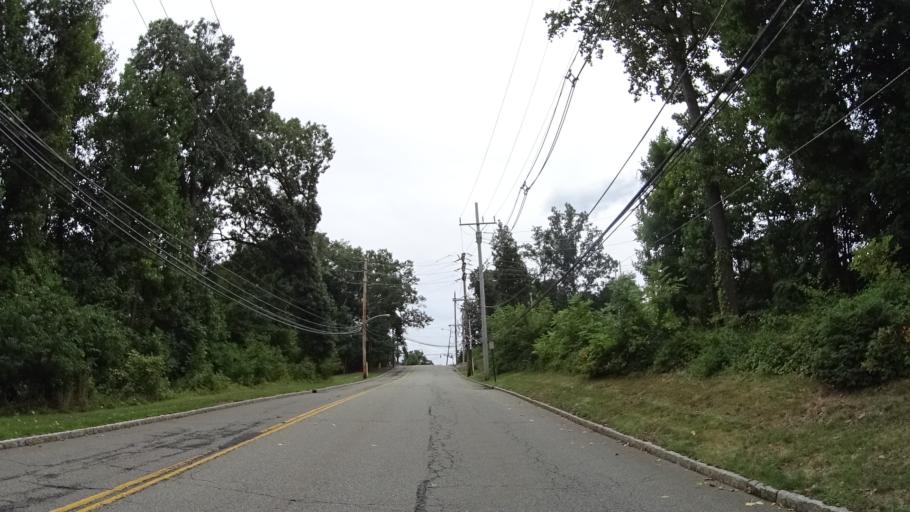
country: US
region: New Jersey
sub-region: Union County
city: New Providence
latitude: 40.6863
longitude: -74.4053
